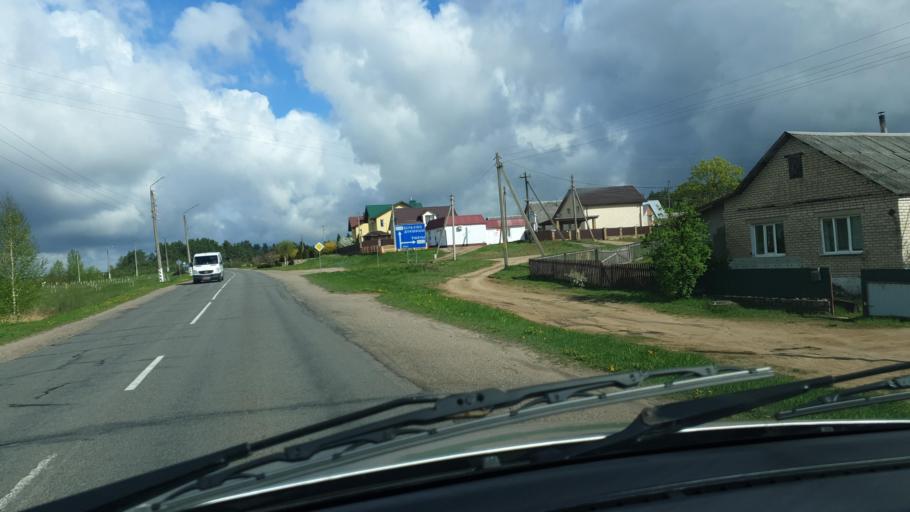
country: BY
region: Vitebsk
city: Lyepyel'
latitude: 54.8811
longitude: 28.6577
